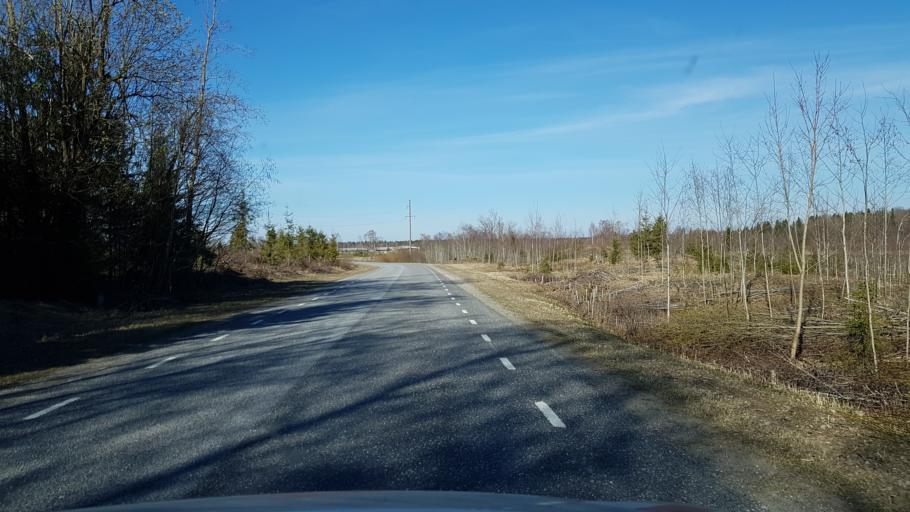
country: EE
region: Laeaene-Virumaa
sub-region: Rakke vald
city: Rakke
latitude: 58.9922
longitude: 26.2709
